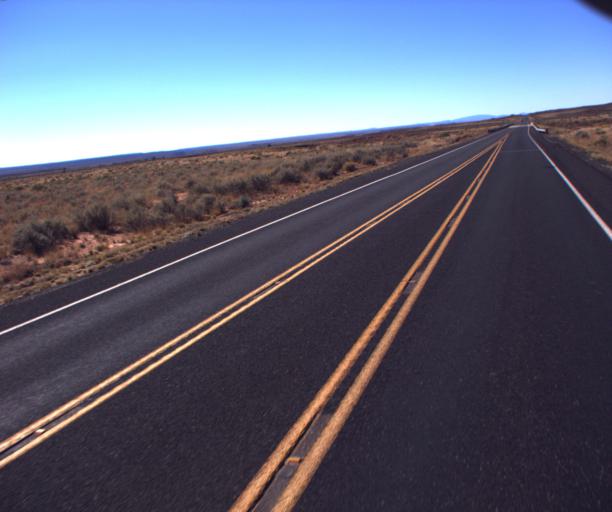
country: US
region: Arizona
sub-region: Coconino County
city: Fredonia
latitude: 36.9299
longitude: -112.5618
